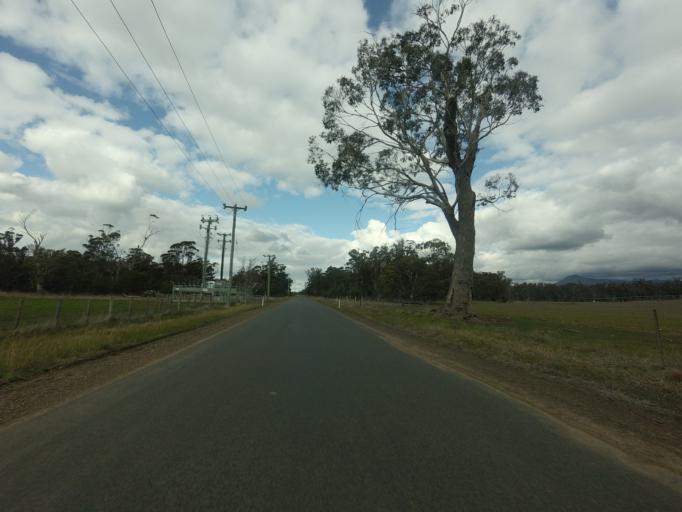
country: AU
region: Tasmania
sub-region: Northern Midlands
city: Longford
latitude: -41.7962
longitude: 147.1211
